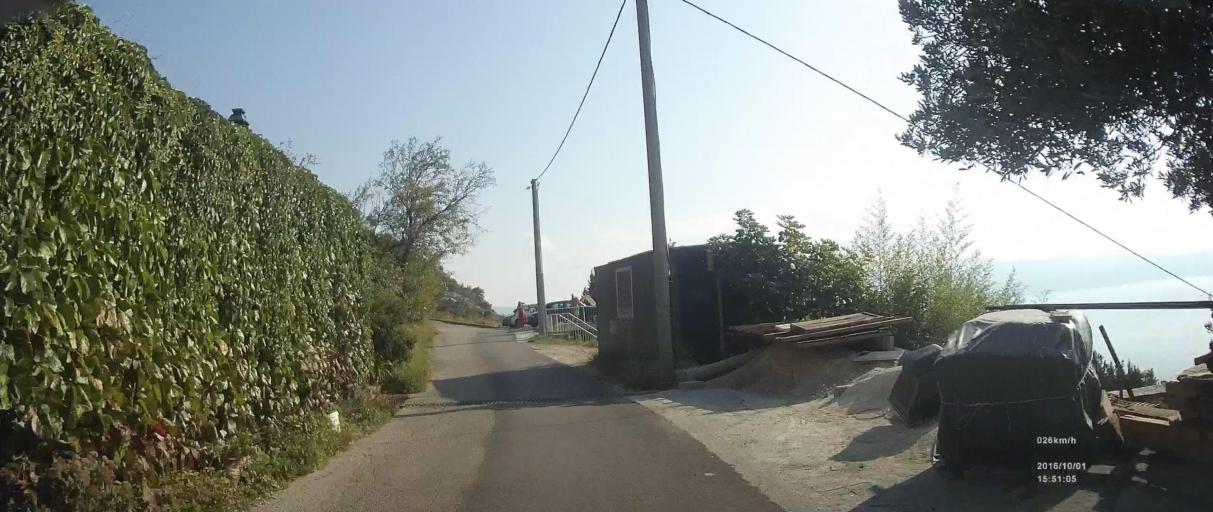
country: HR
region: Splitsko-Dalmatinska
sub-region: Grad Omis
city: Omis
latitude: 43.4394
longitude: 16.7051
